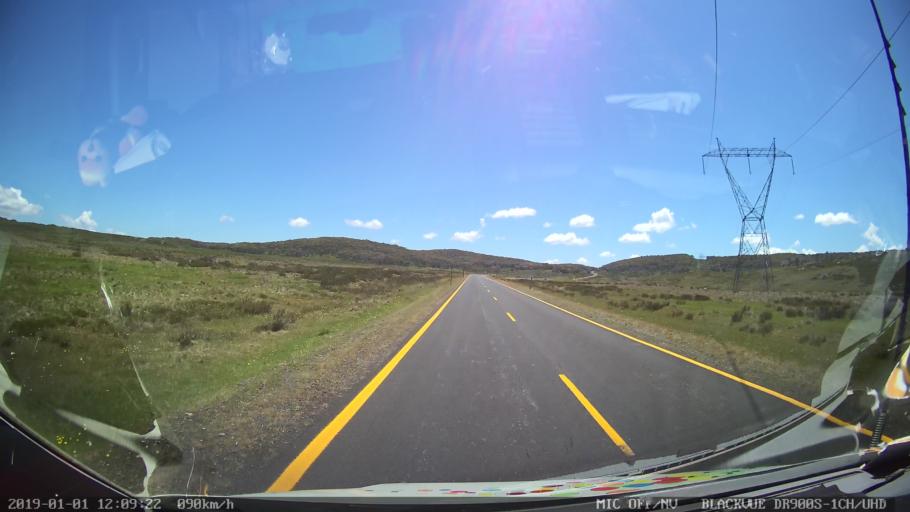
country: AU
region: New South Wales
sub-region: Tumut Shire
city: Tumut
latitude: -35.8080
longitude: 148.4961
